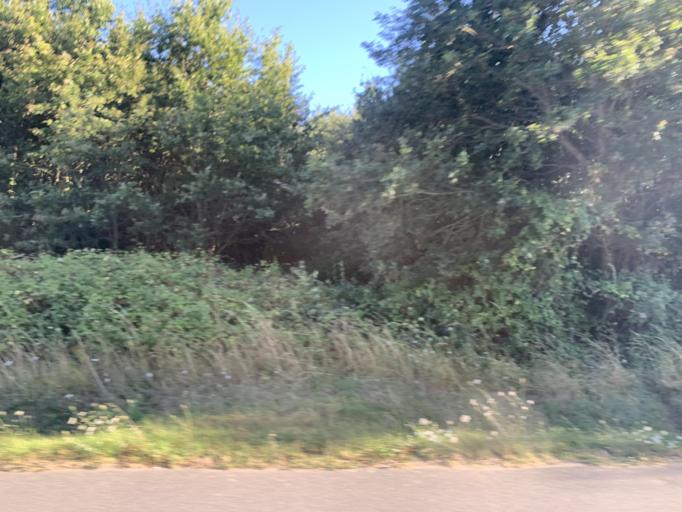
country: FR
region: Pays de la Loire
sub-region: Departement de la Loire-Atlantique
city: Pornichet
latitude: 47.2591
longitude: -2.2794
